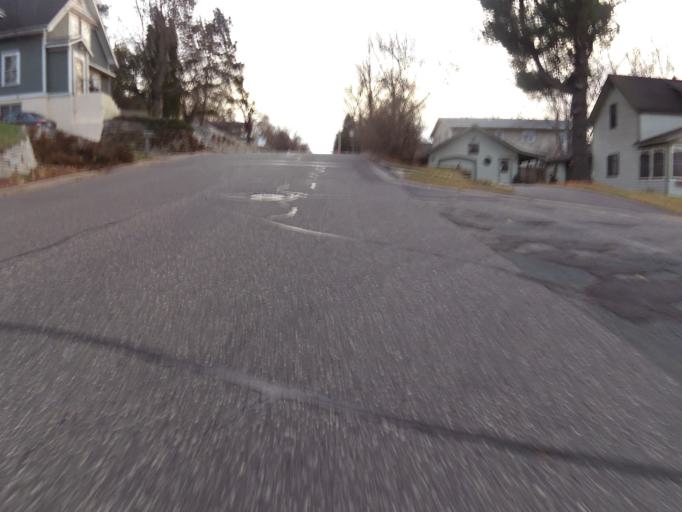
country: US
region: Wisconsin
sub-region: Saint Croix County
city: Hudson
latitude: 44.9814
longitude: -92.7440
